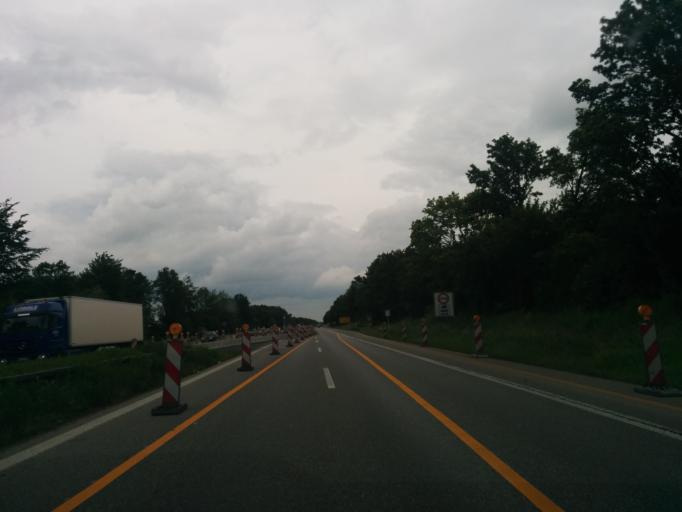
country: DE
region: Bavaria
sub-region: Swabia
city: Konigsbrunn
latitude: 48.2785
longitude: 10.8707
